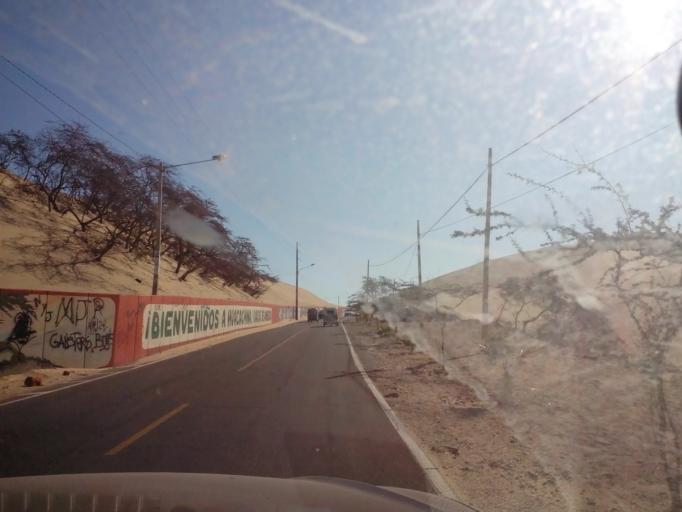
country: PE
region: Ica
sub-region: Provincia de Ica
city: Ica
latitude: -14.0869
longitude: -75.7583
